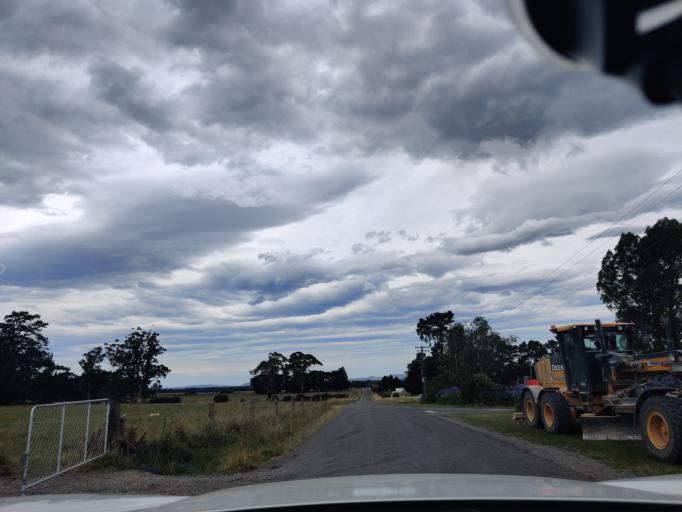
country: NZ
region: Wellington
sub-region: Masterton District
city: Masterton
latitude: -41.0368
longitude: 175.4230
